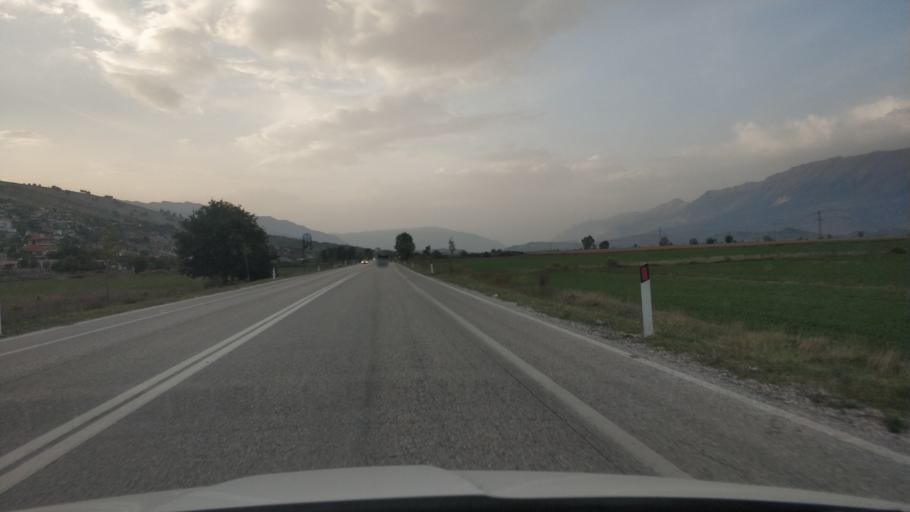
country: AL
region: Gjirokaster
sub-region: Rrethi i Gjirokastres
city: Libohove
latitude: 39.9825
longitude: 20.2275
